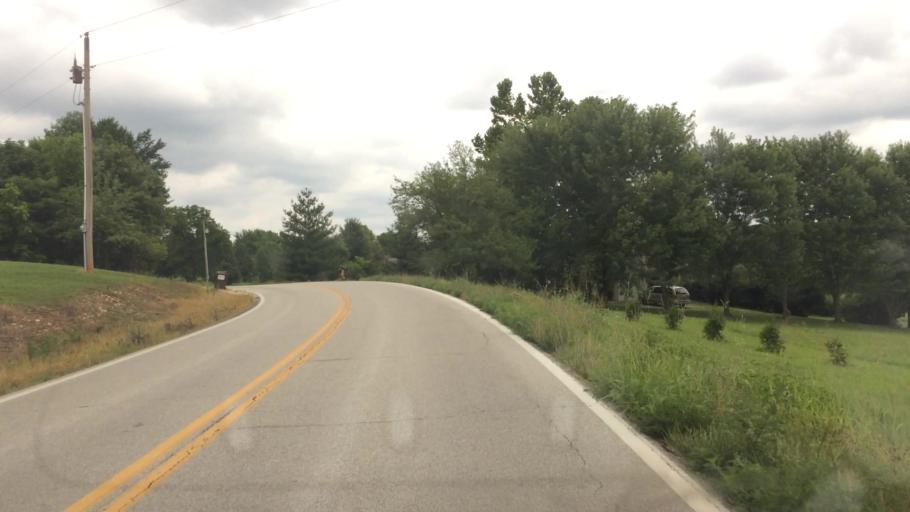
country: US
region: Missouri
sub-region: Greene County
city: Strafford
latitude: 37.2995
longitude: -93.0803
